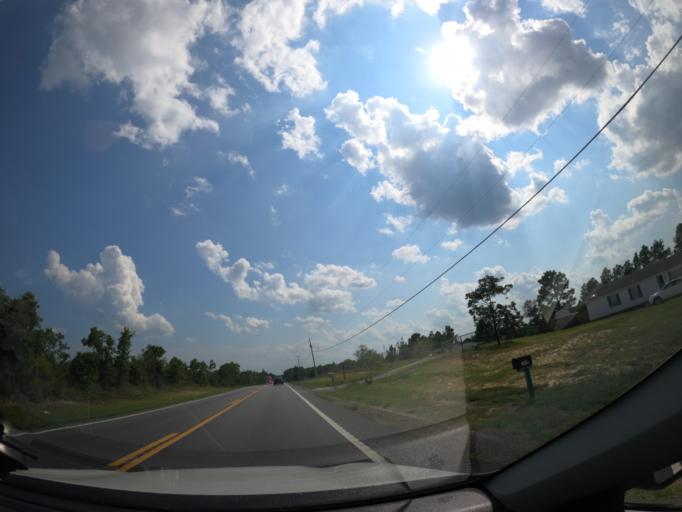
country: US
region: South Carolina
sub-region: Lexington County
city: Red Bank
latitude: 33.8264
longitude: -81.2175
